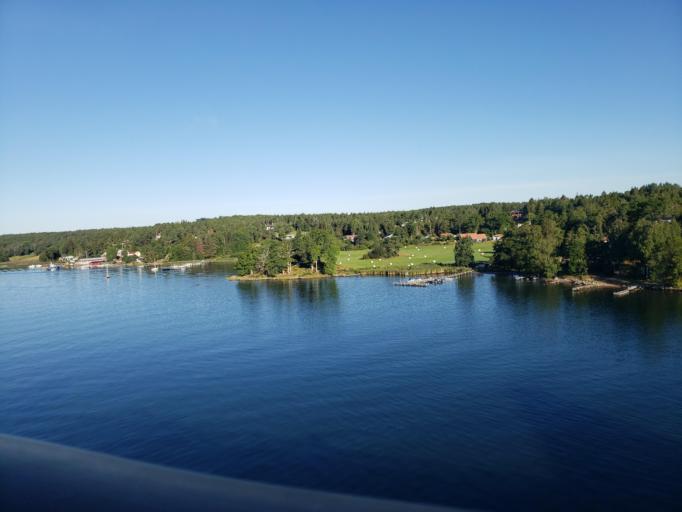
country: SE
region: Stockholm
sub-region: Vaxholms Kommun
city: Vaxholm
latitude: 59.5035
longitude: 18.4747
